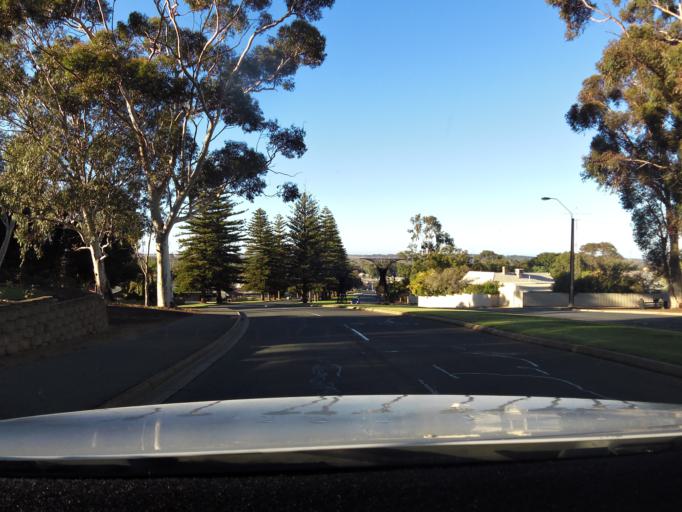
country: AU
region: South Australia
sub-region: Berri and Barmera
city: Berri
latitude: -34.2825
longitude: 140.6000
